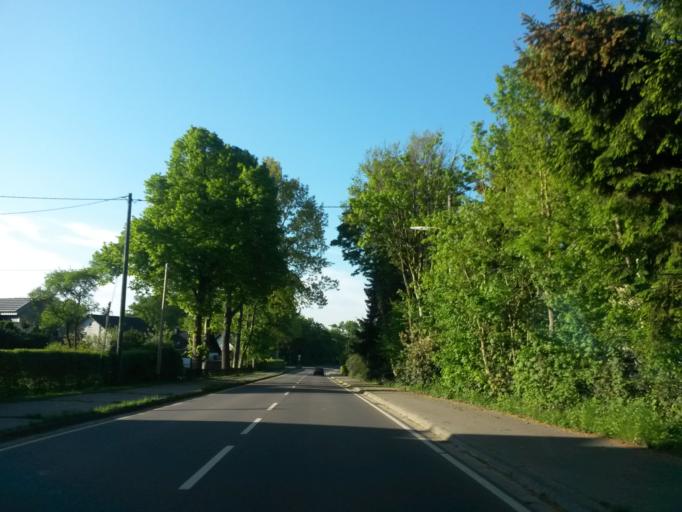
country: DE
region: North Rhine-Westphalia
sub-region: Regierungsbezirk Koln
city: Numbrecht
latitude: 50.9198
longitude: 7.4940
